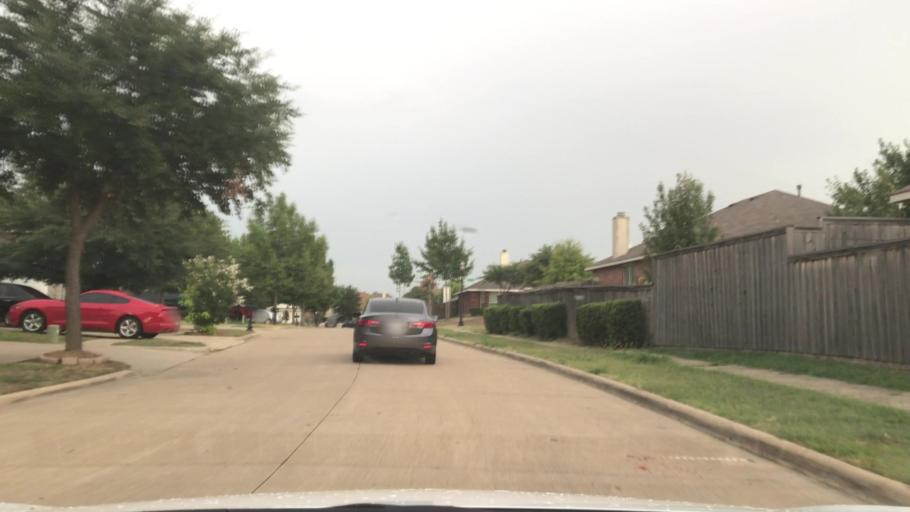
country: US
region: Texas
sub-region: Kaufman County
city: Forney
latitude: 32.7213
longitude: -96.5370
